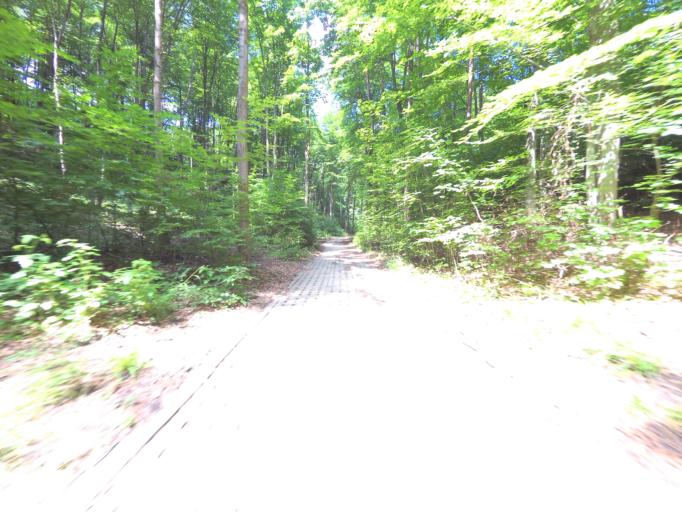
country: PL
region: Pomeranian Voivodeship
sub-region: Gdynia
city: Wielki Kack
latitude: 54.4893
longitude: 18.5071
